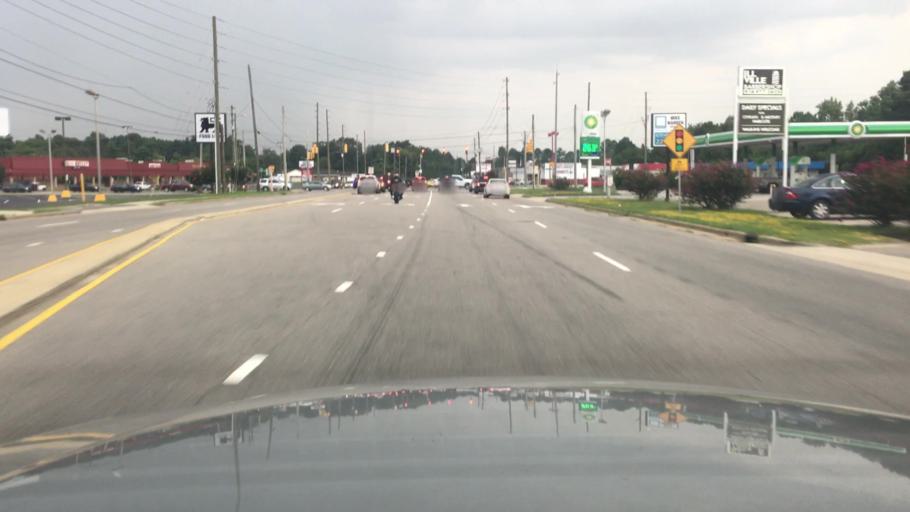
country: US
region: North Carolina
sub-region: Cumberland County
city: Fort Bragg
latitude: 35.0839
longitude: -79.0103
